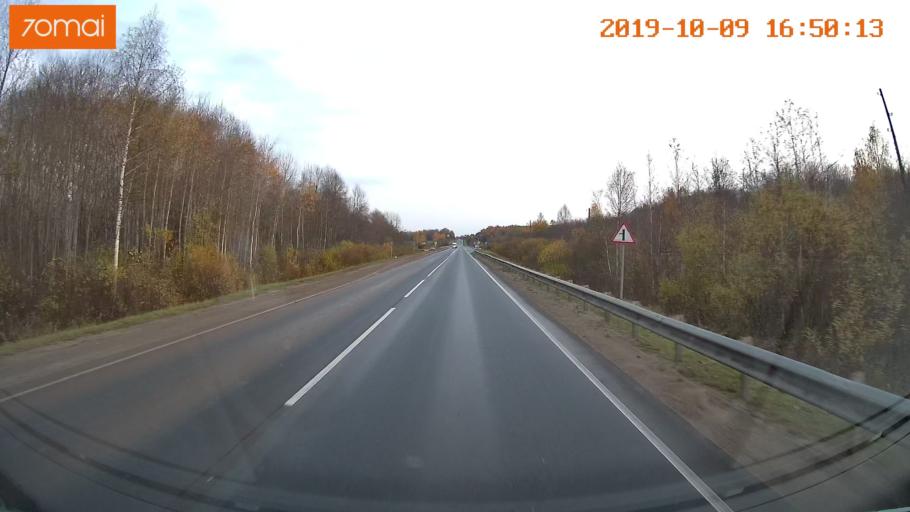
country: RU
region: Kostroma
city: Volgorechensk
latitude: 57.4042
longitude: 41.2058
